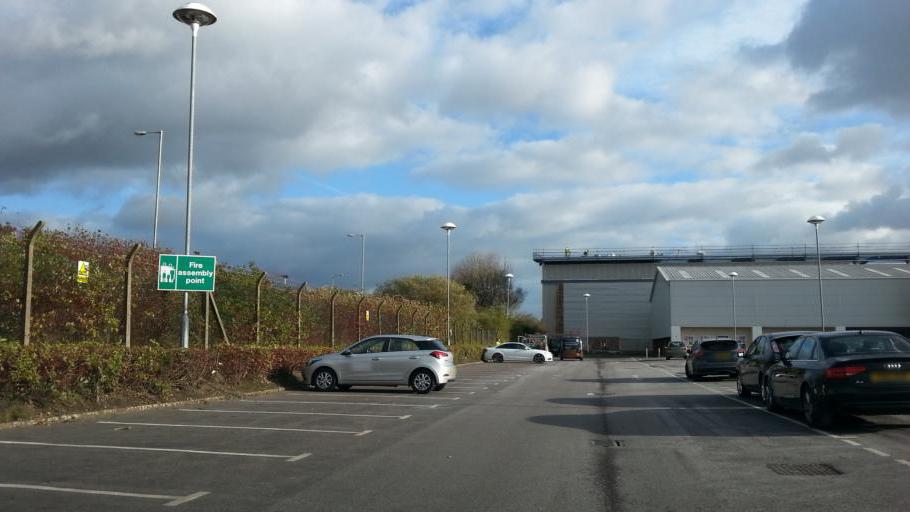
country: GB
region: England
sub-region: Staffordshire
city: Cannock
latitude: 52.6788
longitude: -2.0472
